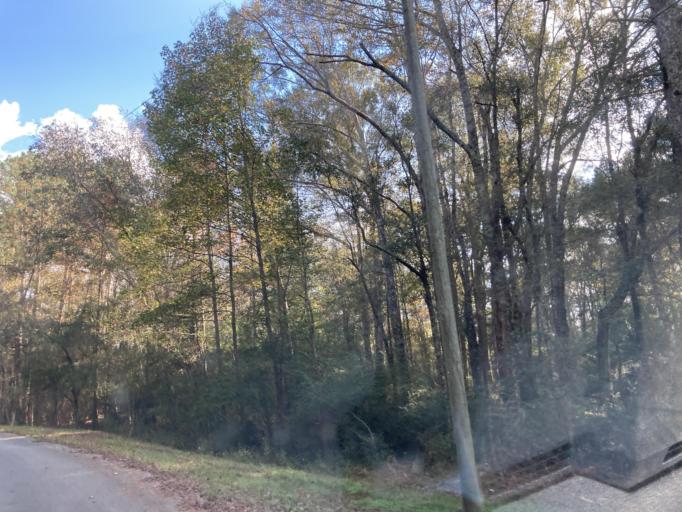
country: US
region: Mississippi
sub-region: Lamar County
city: Sumrall
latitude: 31.4462
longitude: -89.5868
